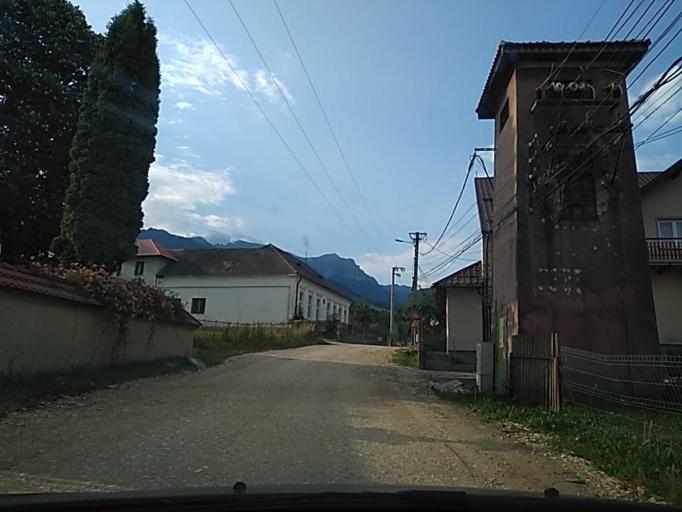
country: RO
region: Brasov
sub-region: Comuna Bran
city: Sohodol
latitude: 45.5037
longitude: 25.3826
